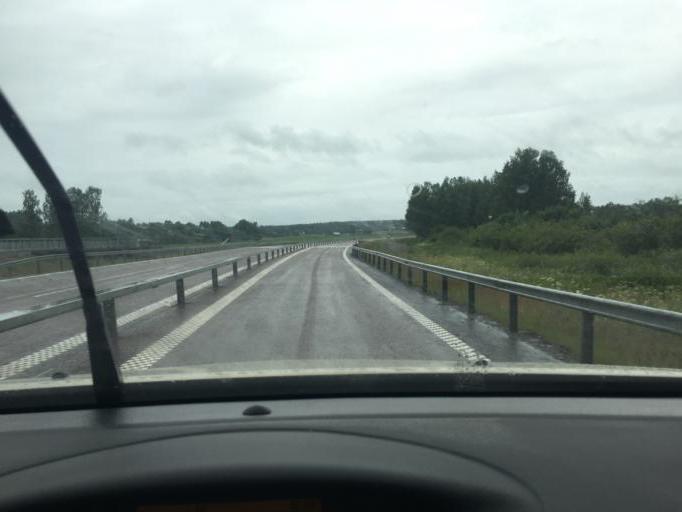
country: SE
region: Norrbotten
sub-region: Kalix Kommun
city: Rolfs
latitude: 65.8703
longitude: 23.0438
